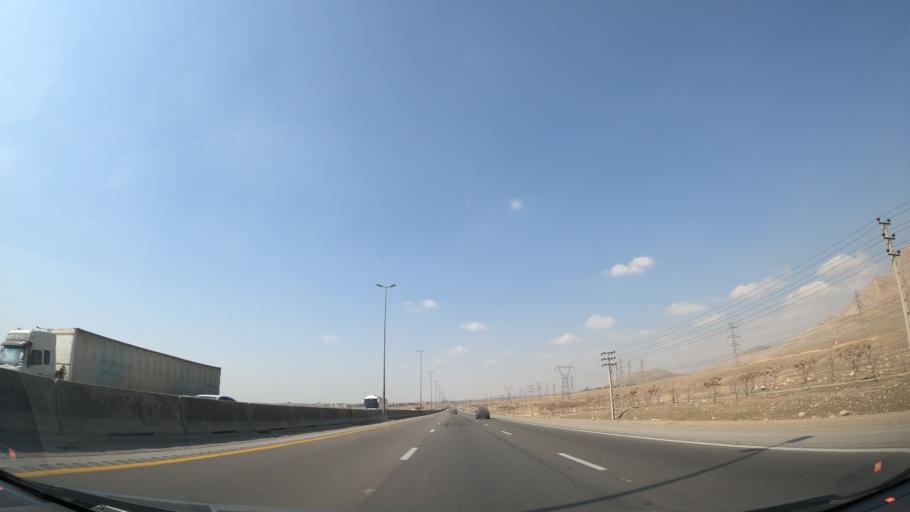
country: IR
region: Qazvin
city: Abyek
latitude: 36.0561
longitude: 50.5069
